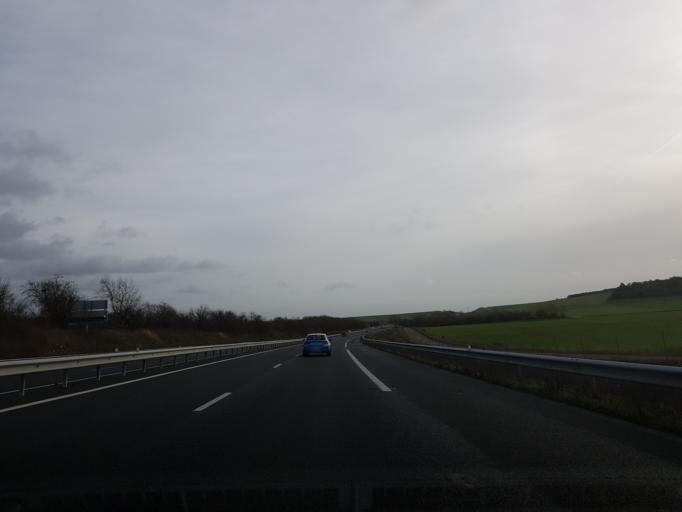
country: FR
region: Champagne-Ardenne
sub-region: Departement de l'Aube
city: La Riviere-de-Corps
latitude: 48.2687
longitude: 3.9612
